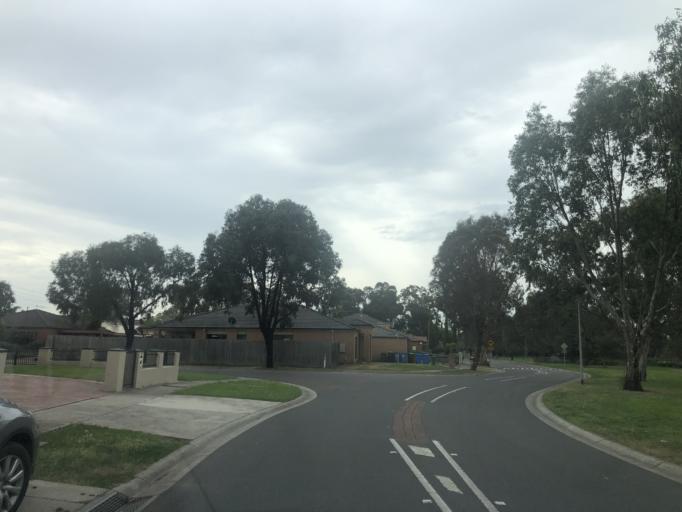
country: AU
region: Victoria
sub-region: Casey
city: Hallam
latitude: -38.0021
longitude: 145.2880
